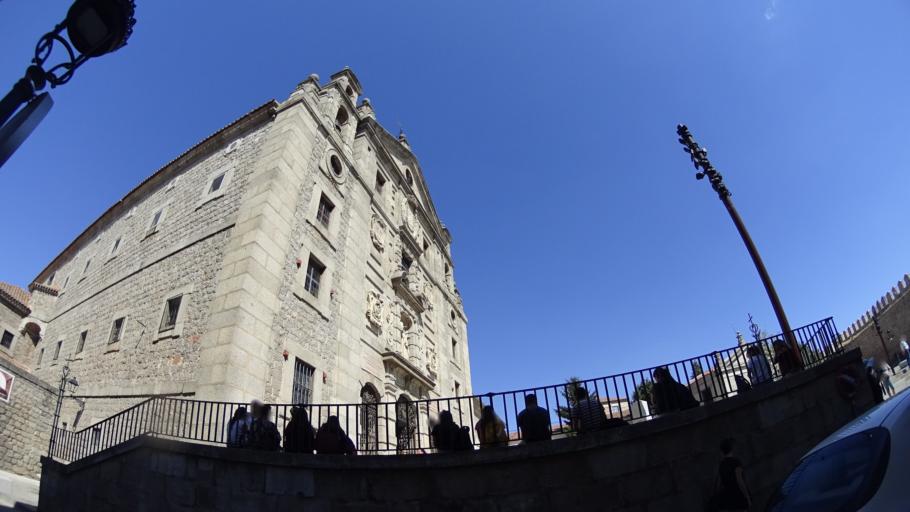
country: ES
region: Castille and Leon
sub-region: Provincia de Avila
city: Avila
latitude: 40.6552
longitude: -4.7030
